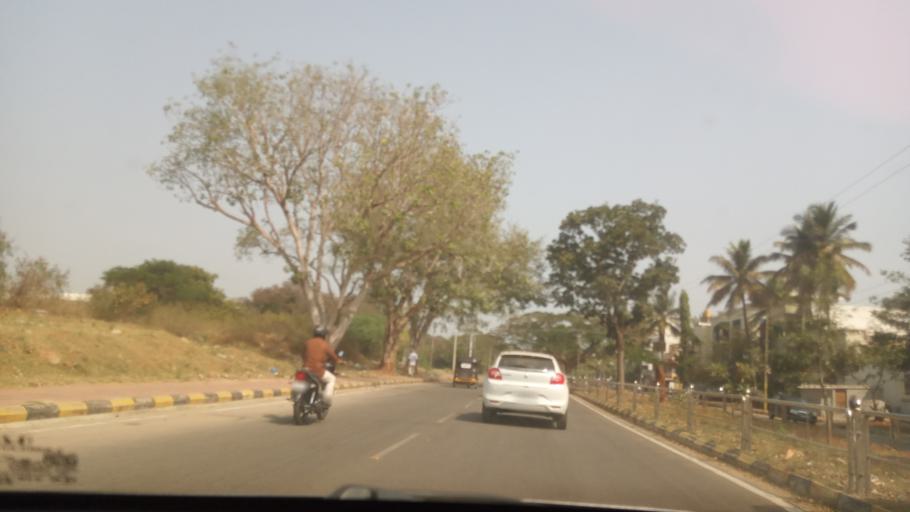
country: IN
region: Karnataka
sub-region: Mysore
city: Mysore
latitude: 12.3030
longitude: 76.6266
